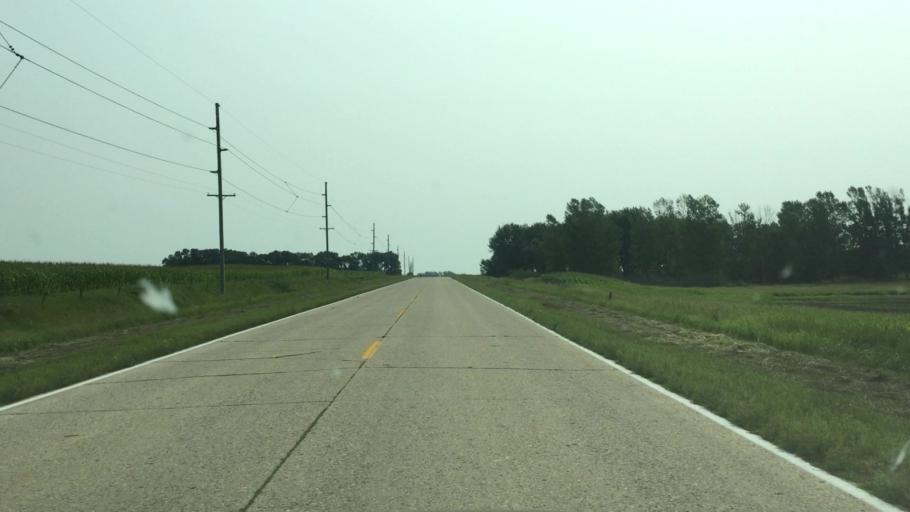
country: US
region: Iowa
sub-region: Dickinson County
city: Milford
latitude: 43.3714
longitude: -95.1990
